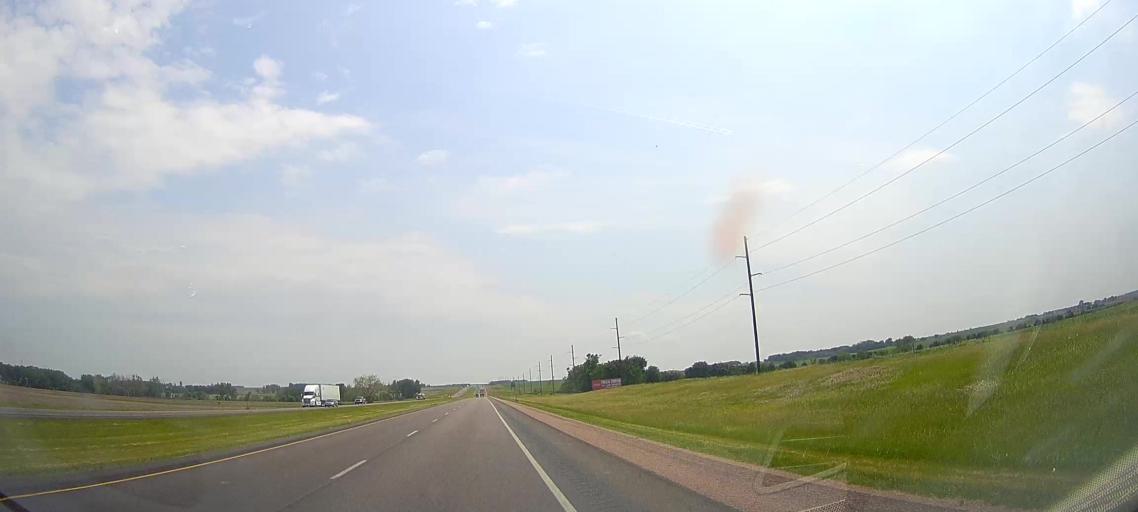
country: US
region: South Dakota
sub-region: Union County
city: Beresford
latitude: 43.1880
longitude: -96.7954
